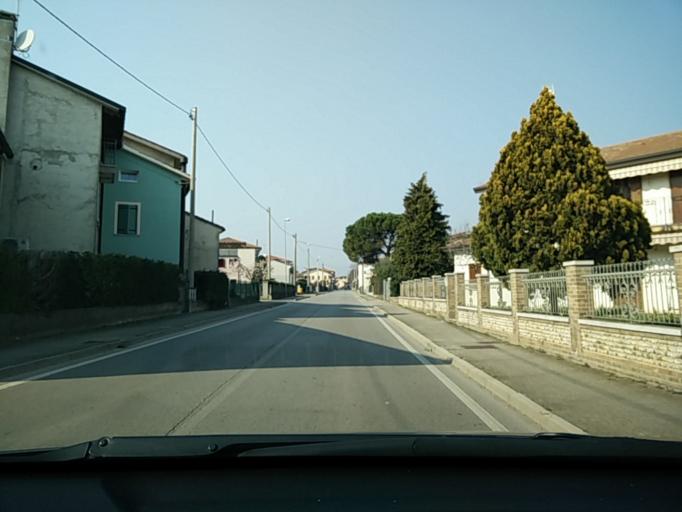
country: IT
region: Veneto
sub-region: Provincia di Treviso
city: Camalo
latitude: 45.7494
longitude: 12.1711
